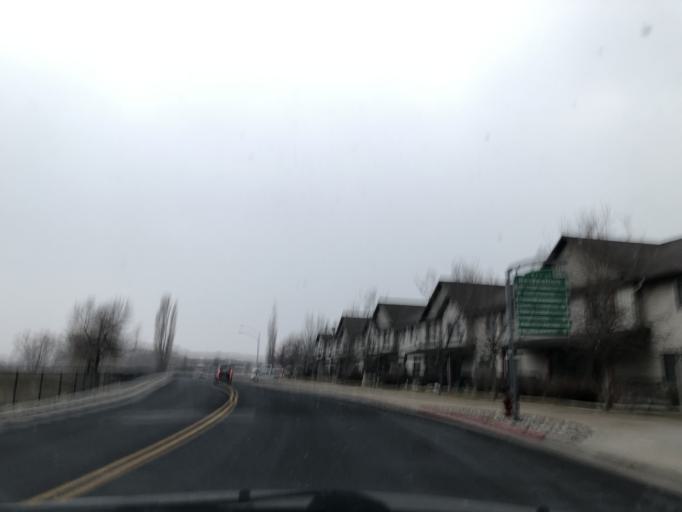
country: US
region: Utah
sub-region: Cache County
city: Logan
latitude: 41.7148
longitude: -111.8466
